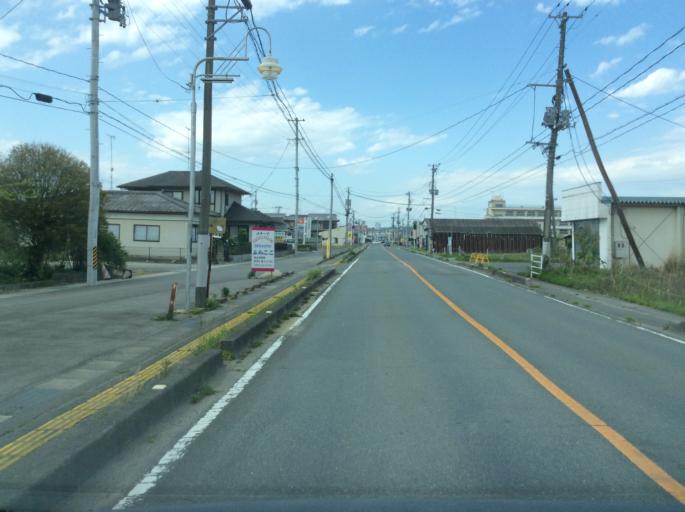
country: JP
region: Ibaraki
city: Kitaibaraki
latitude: 36.9005
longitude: 140.7859
